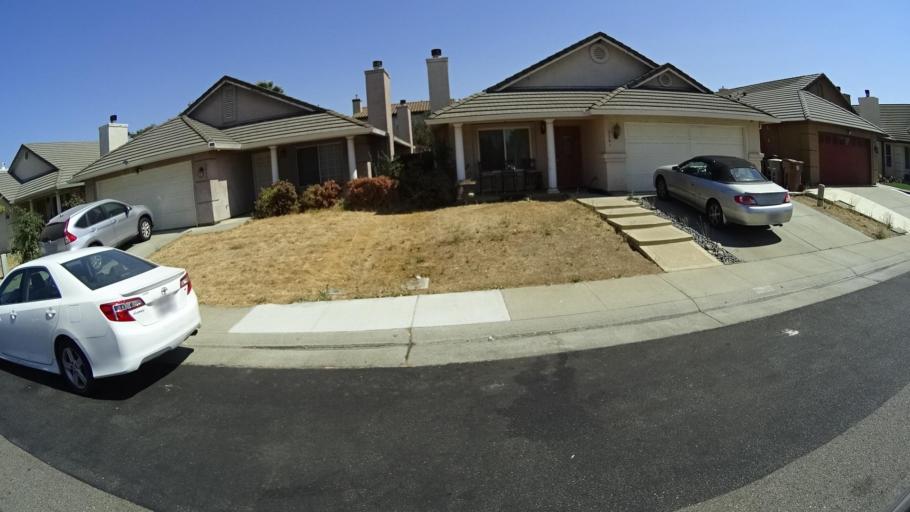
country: US
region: California
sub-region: Sacramento County
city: Laguna
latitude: 38.4184
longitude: -121.4093
